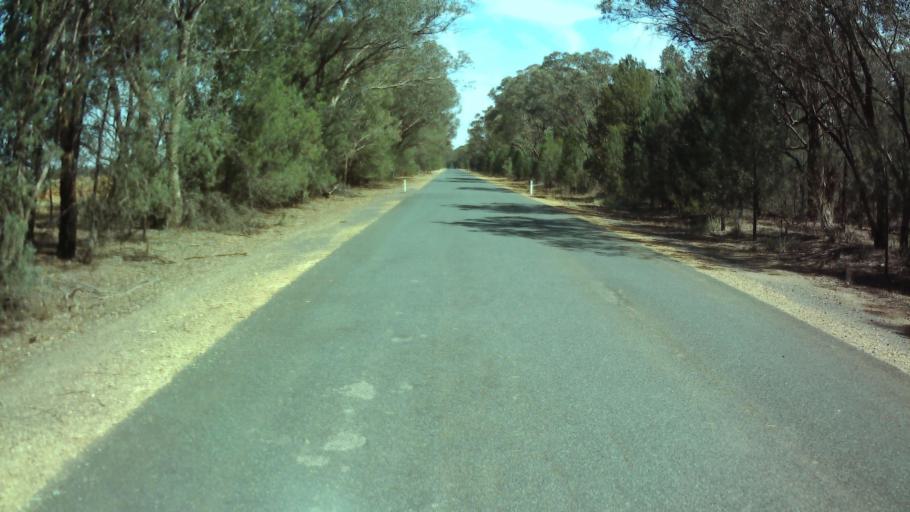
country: AU
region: New South Wales
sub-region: Weddin
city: Grenfell
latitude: -34.0168
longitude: 148.1293
